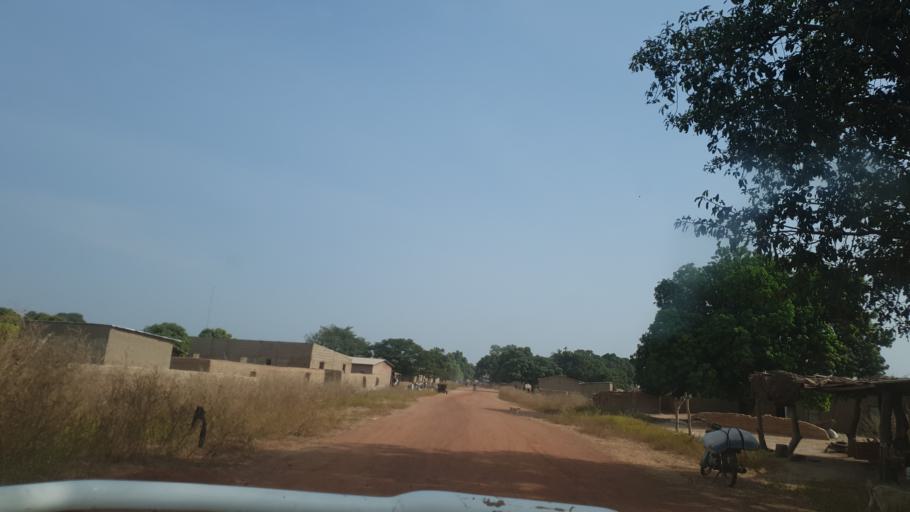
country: ML
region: Koulikoro
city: Dioila
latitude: 12.2199
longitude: -6.2100
